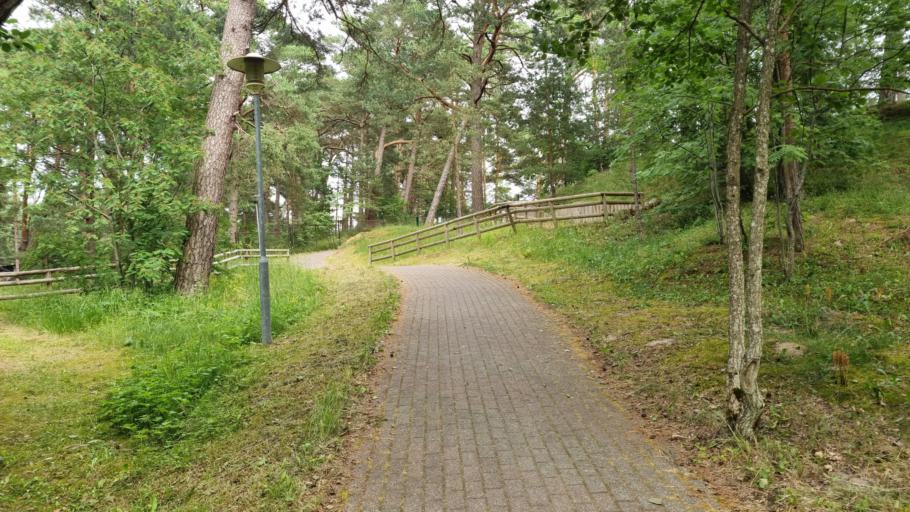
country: LV
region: Ventspils
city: Ventspils
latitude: 57.3849
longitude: 21.5324
